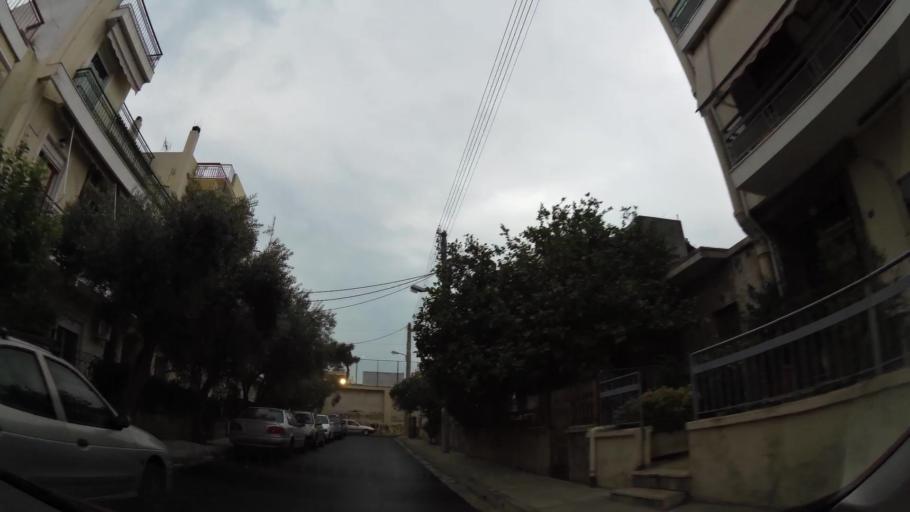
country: GR
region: Attica
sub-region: Nomarchia Athinas
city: Agioi Anargyroi
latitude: 38.0401
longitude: 23.7262
